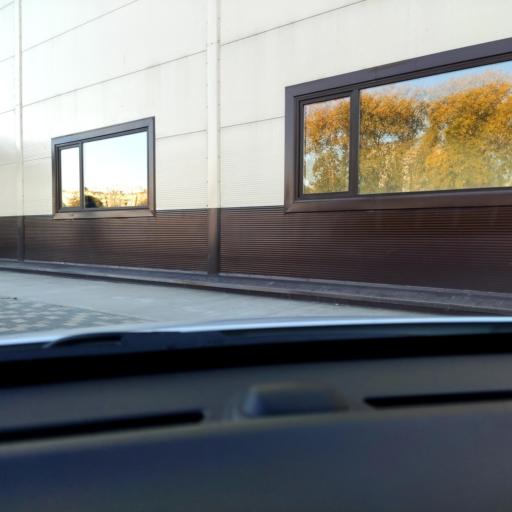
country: RU
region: Voronezj
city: Voronezh
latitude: 51.6738
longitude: 39.2394
